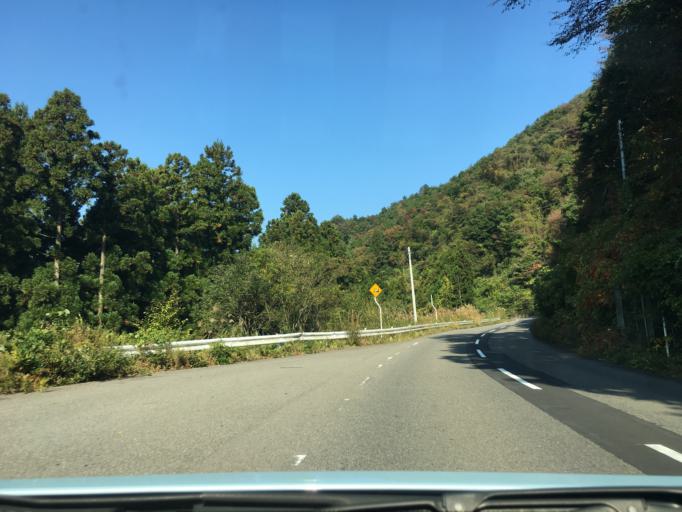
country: JP
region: Fukushima
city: Sukagawa
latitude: 37.2987
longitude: 140.1581
